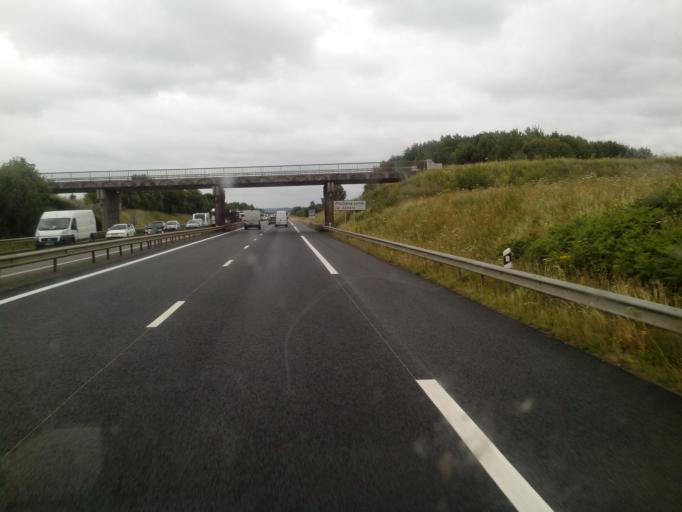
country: FR
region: Brittany
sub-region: Departement d'Ille-et-Vilaine
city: Chatillon-sur-Seiche
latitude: 48.0628
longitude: -1.6785
